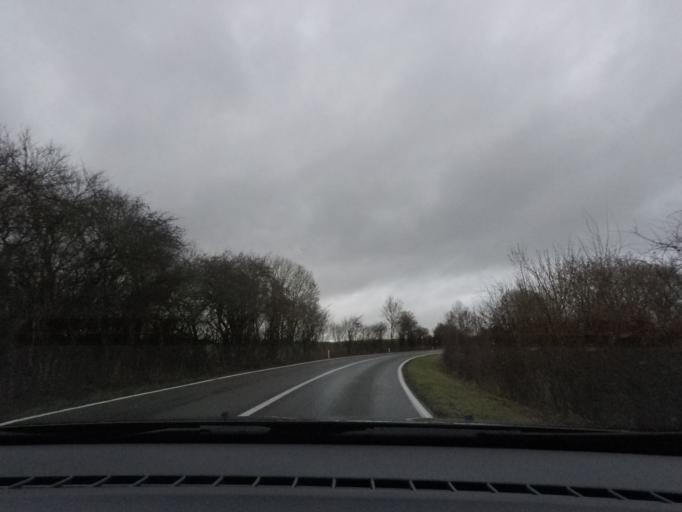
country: BE
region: Wallonia
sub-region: Province du Luxembourg
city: Tintigny
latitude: 49.6997
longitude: 5.5278
